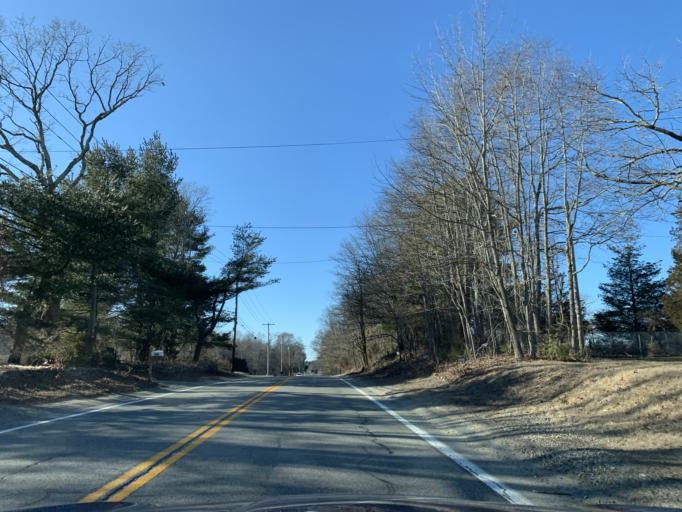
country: US
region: Rhode Island
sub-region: Providence County
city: North Providence
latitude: 41.8864
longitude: -71.4844
